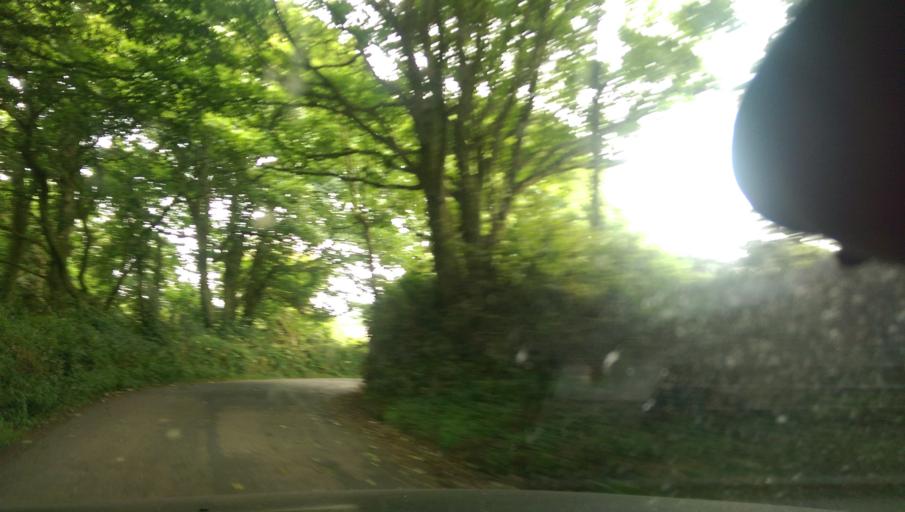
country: GB
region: England
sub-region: Cornwall
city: St. Buryan
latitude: 50.0977
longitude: -5.6145
